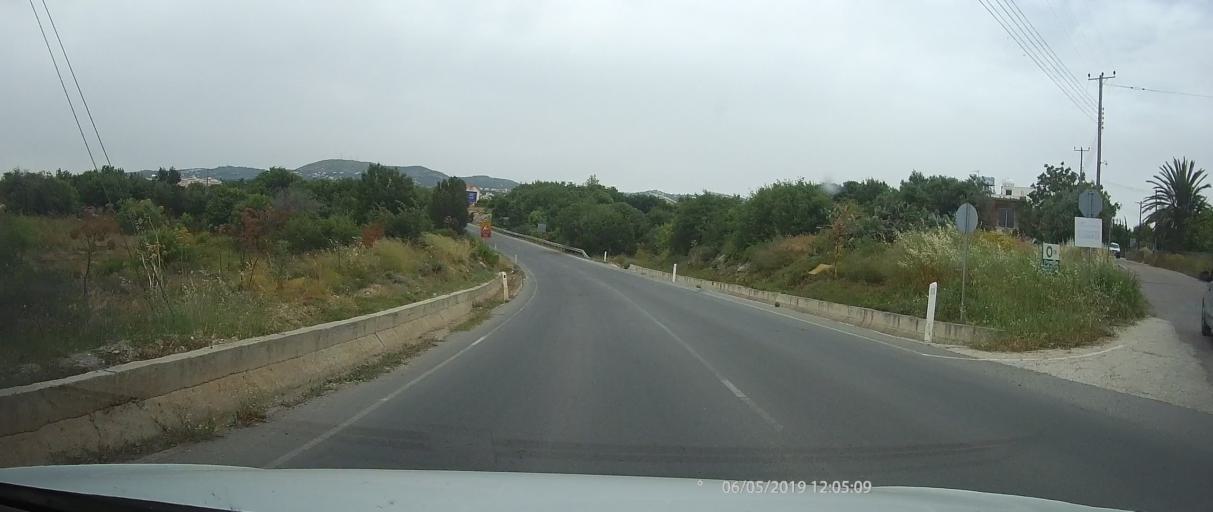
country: CY
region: Pafos
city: Empa
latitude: 34.8047
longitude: 32.4305
